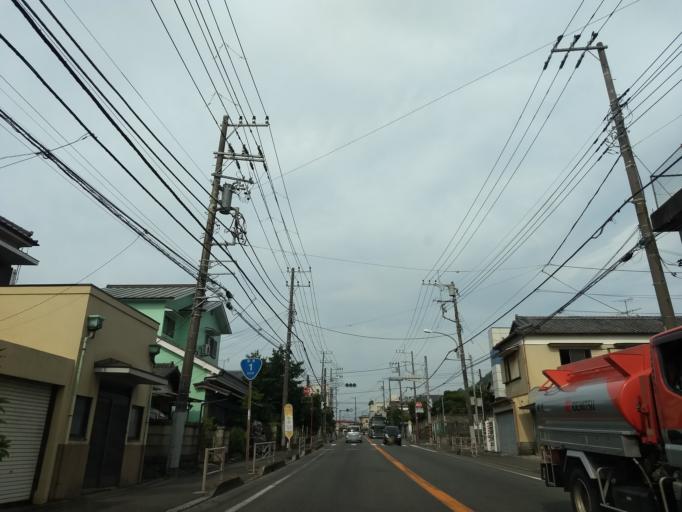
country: JP
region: Kanagawa
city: Ninomiya
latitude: 35.2840
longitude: 139.2247
